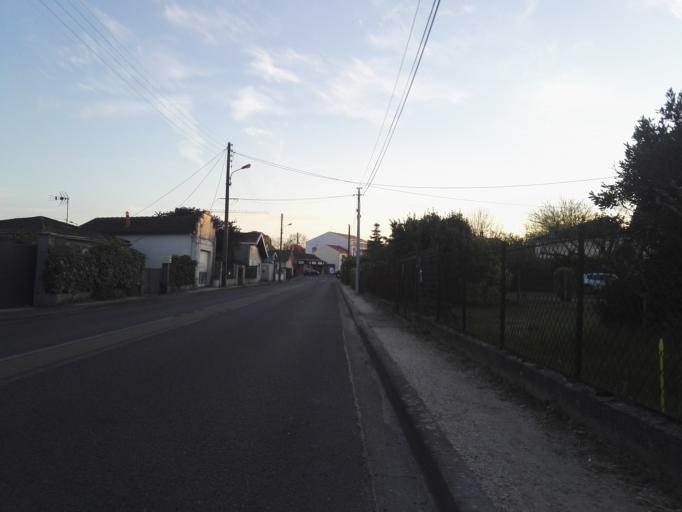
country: FR
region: Aquitaine
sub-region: Departement de la Gironde
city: Pessac
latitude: 44.8104
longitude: -0.6257
